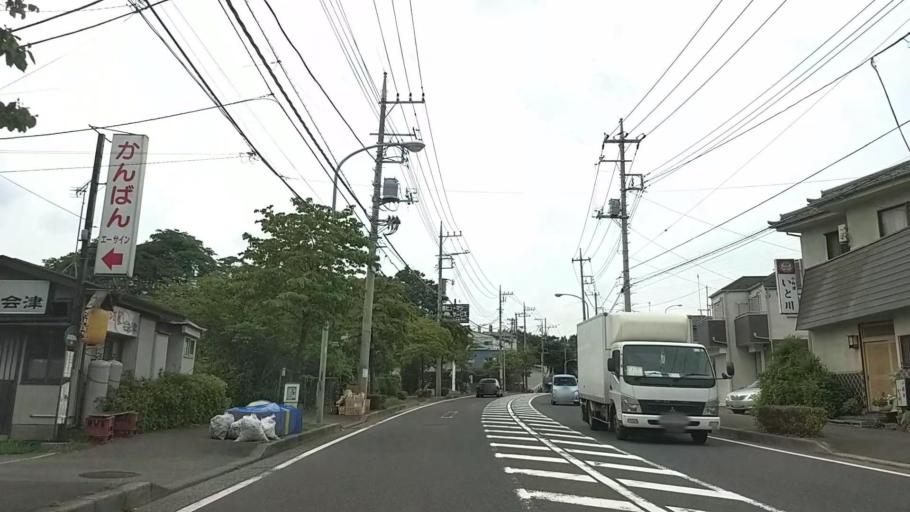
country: JP
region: Kanagawa
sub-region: Kawasaki-shi
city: Kawasaki
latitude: 35.5617
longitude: 139.6105
